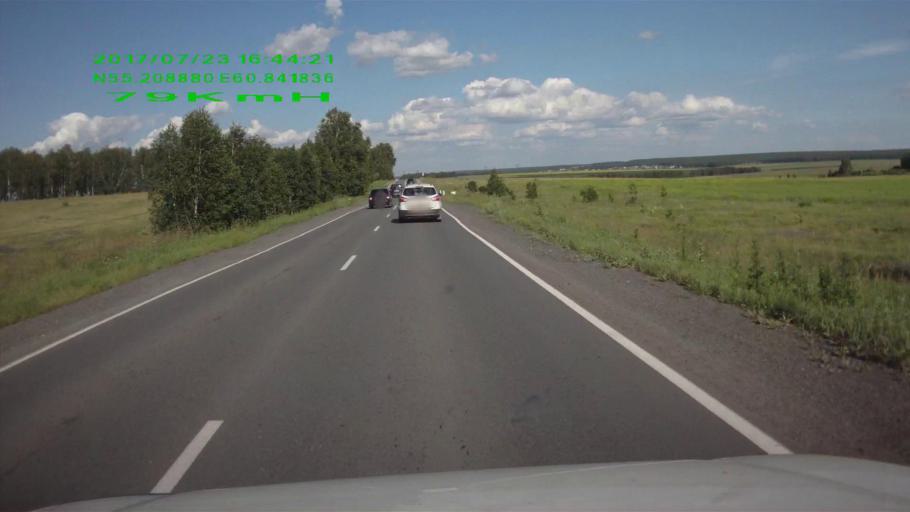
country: RU
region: Chelyabinsk
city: Argayash
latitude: 55.2089
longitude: 60.8410
